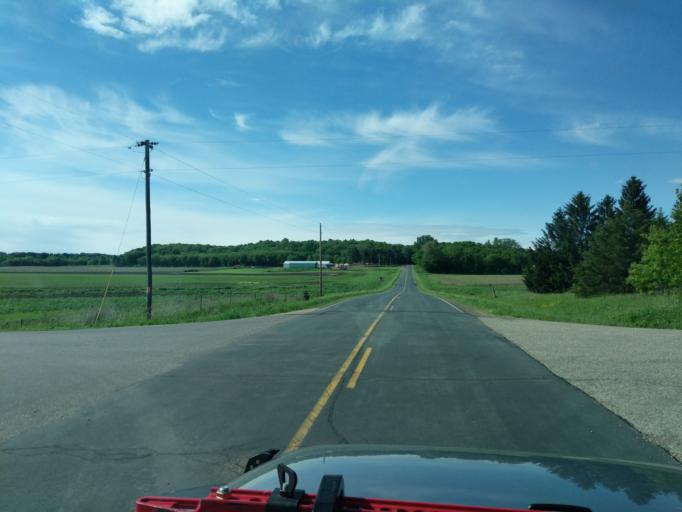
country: US
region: Wisconsin
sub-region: Saint Croix County
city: Hammond
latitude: 44.8878
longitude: -92.4864
